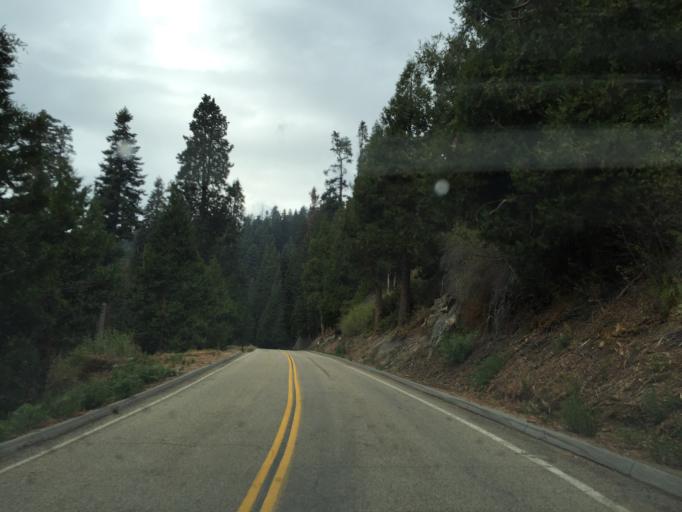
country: US
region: California
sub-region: Tulare County
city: Three Rivers
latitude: 36.7187
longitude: -118.9448
